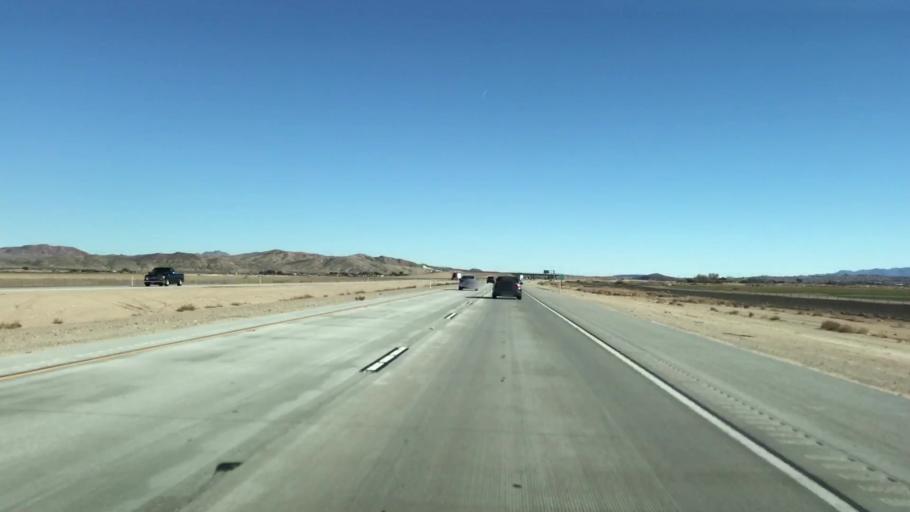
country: US
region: California
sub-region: San Bernardino County
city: Lenwood
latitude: 34.9154
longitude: -117.1348
